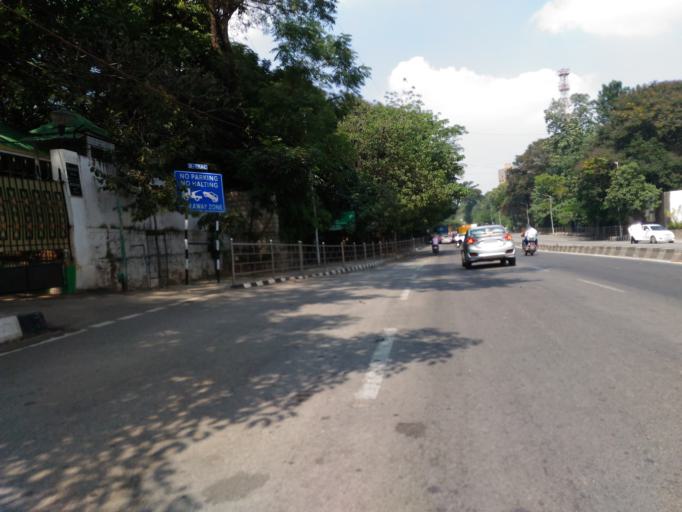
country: IN
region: Karnataka
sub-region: Bangalore Urban
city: Bangalore
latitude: 12.9803
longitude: 77.5857
